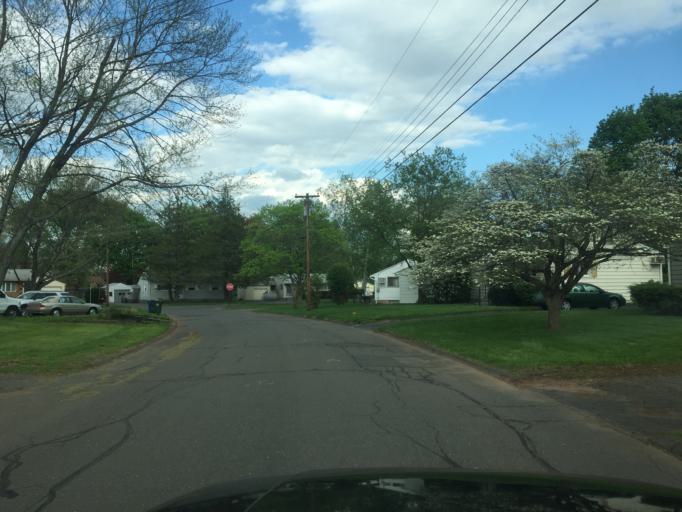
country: US
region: Connecticut
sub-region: Hartford County
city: Kensington
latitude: 41.6235
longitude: -72.7521
